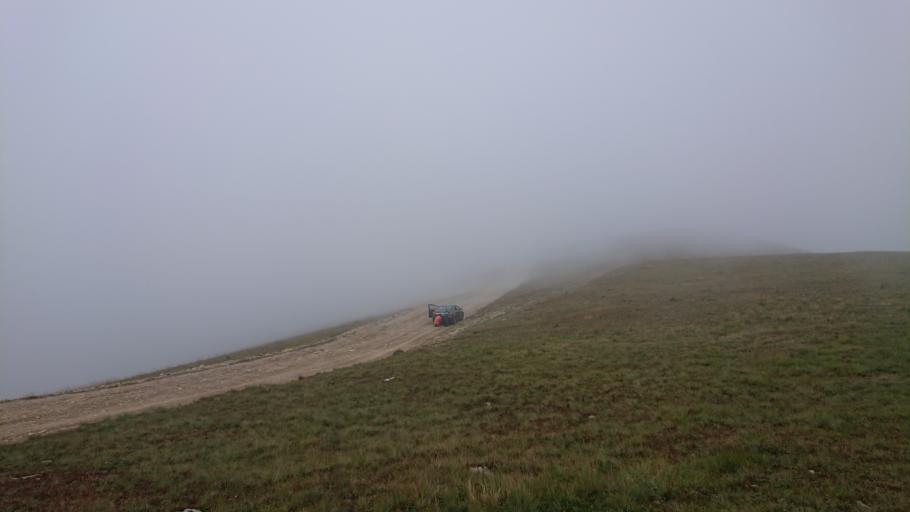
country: TR
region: Gumushane
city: Kurtun
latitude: 40.6233
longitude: 38.9929
